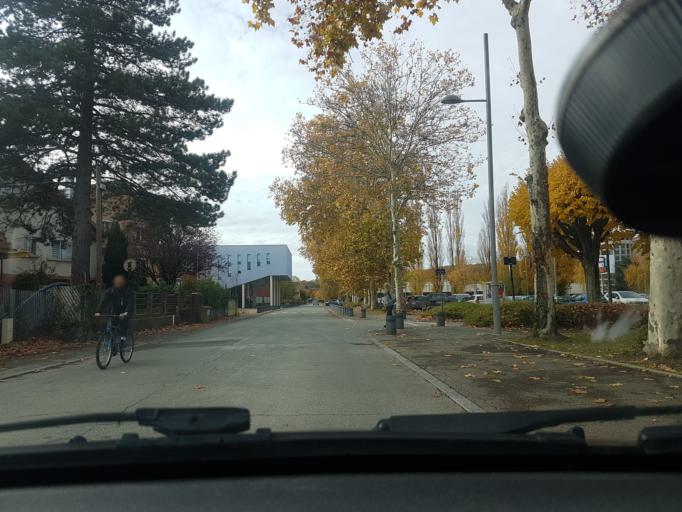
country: FR
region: Franche-Comte
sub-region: Territoire de Belfort
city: Cravanche
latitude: 47.6421
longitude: 6.8459
